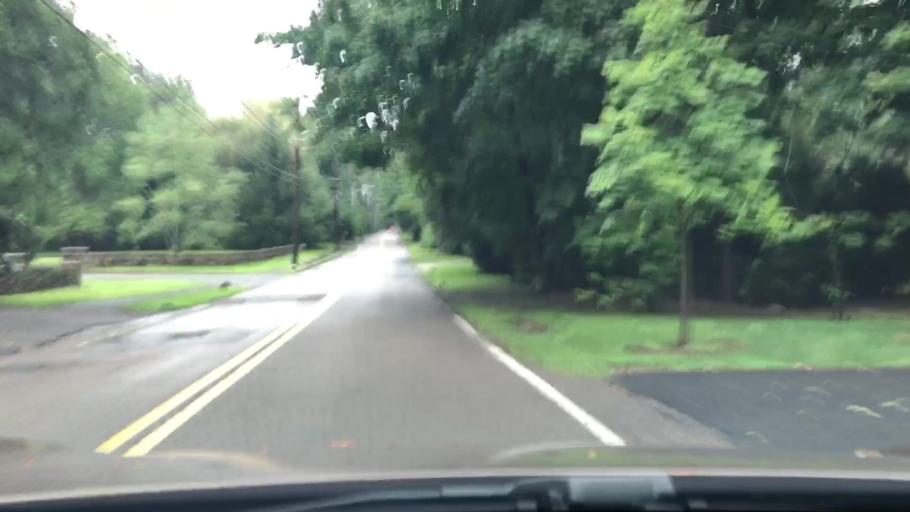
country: US
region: New York
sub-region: Westchester County
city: Scarsdale
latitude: 41.0063
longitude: -73.7761
